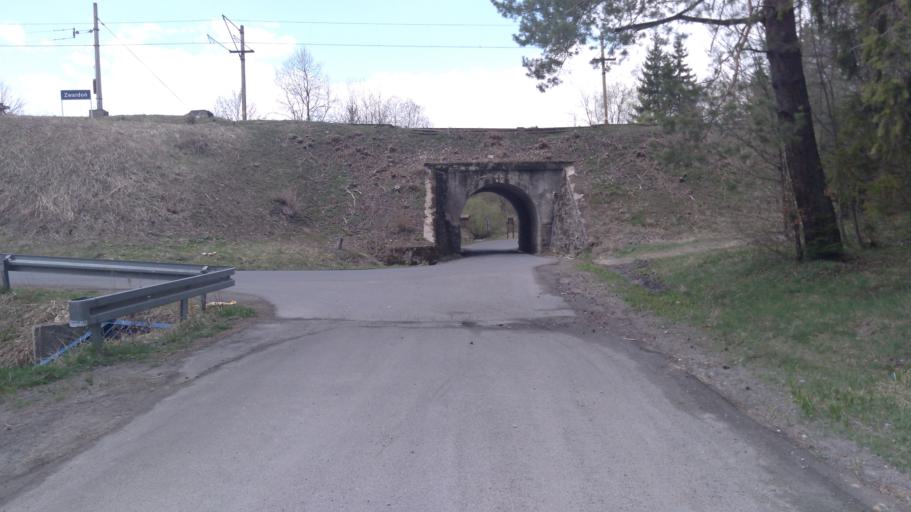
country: PL
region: Silesian Voivodeship
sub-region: Powiat zywiecki
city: Laliki
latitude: 49.5069
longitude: 18.9811
